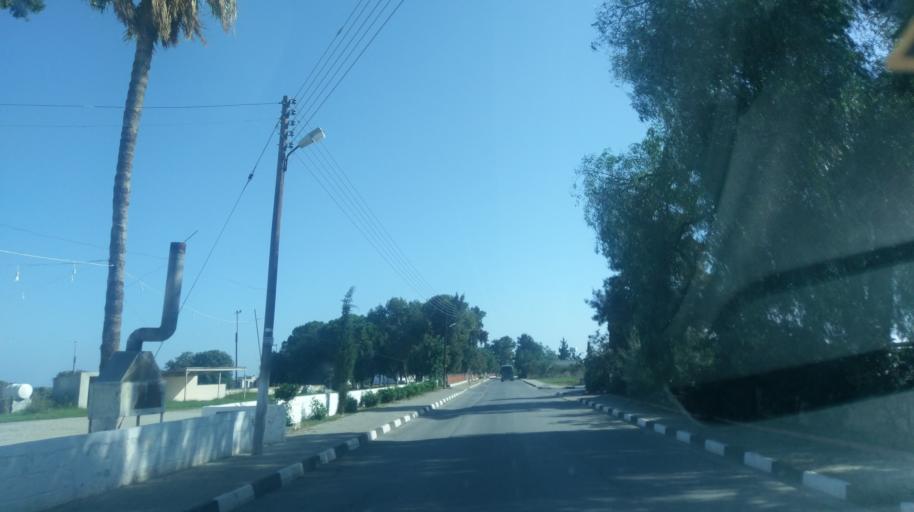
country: CY
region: Ammochostos
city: Trikomo
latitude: 35.2355
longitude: 33.8733
